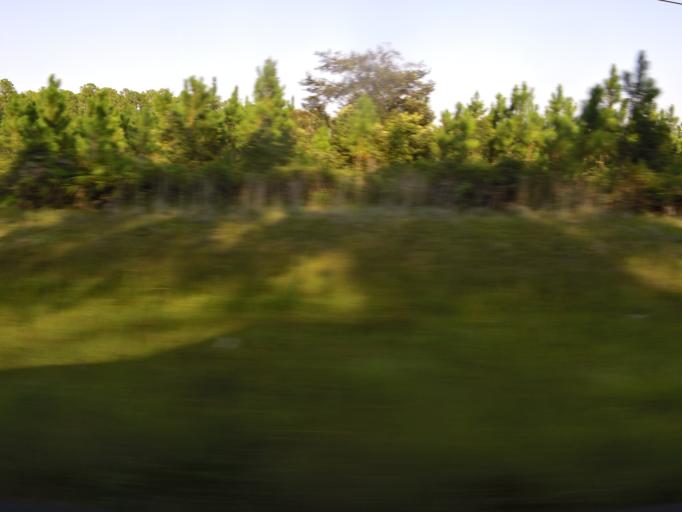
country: US
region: Florida
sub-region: Duval County
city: Baldwin
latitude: 30.3774
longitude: -82.0171
